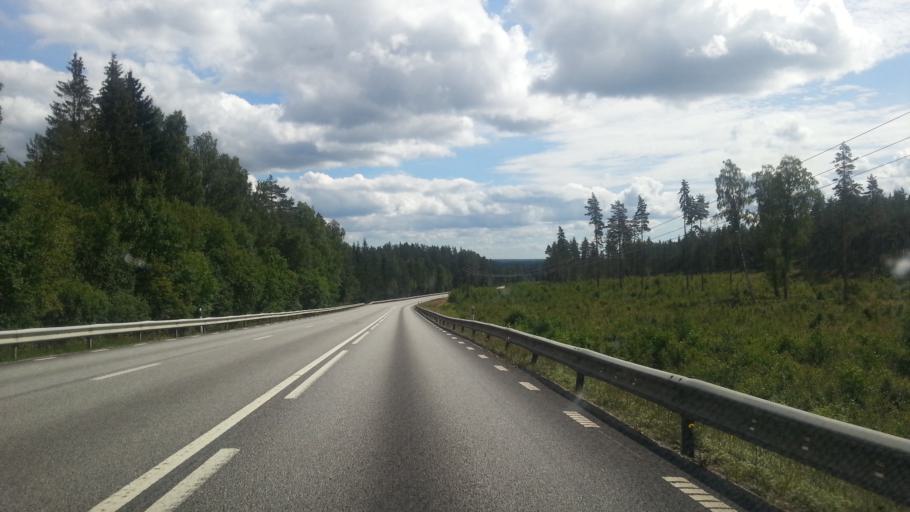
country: SE
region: OErebro
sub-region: Lindesbergs Kommun
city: Stora
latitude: 59.6423
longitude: 15.1425
